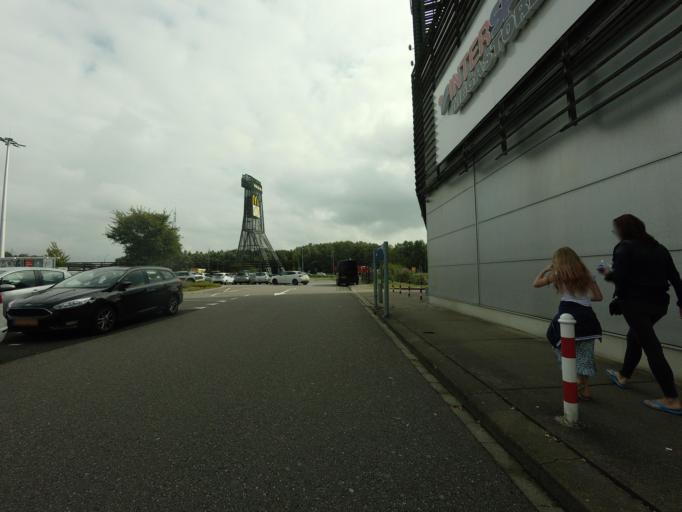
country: NL
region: Overijssel
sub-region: Gemeente Borne
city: Borne
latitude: 52.2877
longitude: 6.7672
